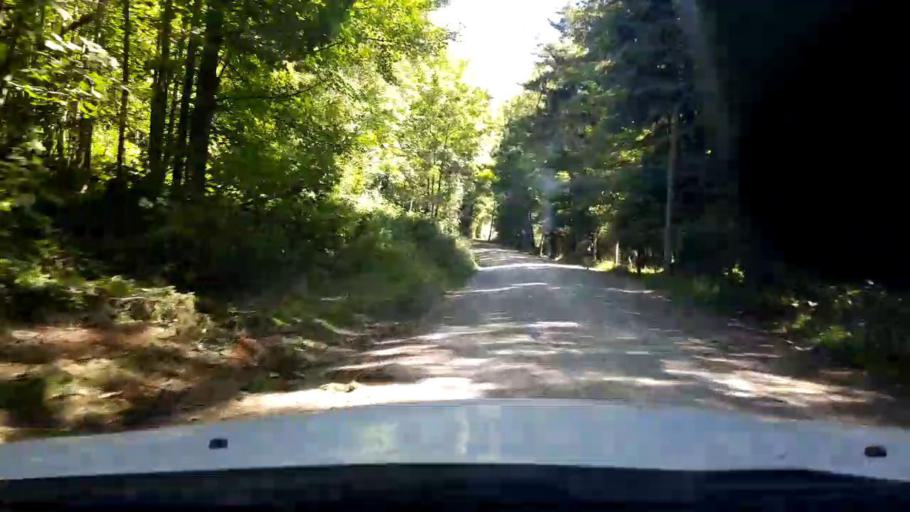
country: NZ
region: Canterbury
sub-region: Timaru District
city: Pleasant Point
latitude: -44.0241
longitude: 170.7439
